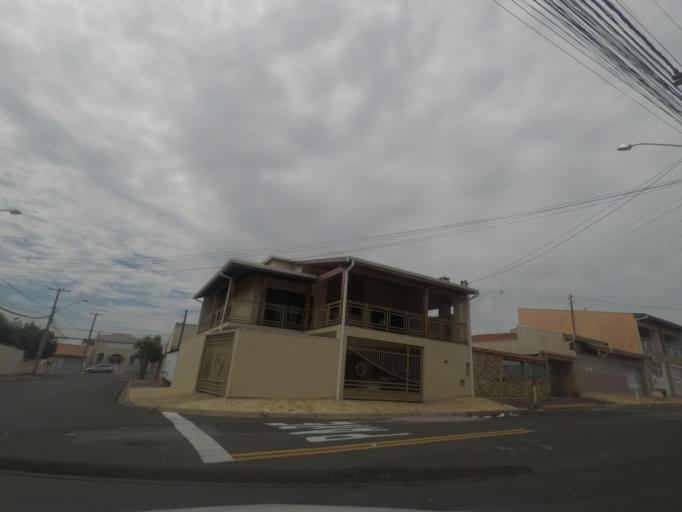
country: BR
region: Sao Paulo
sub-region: Nova Odessa
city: Nova Odessa
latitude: -22.7992
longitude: -47.2808
